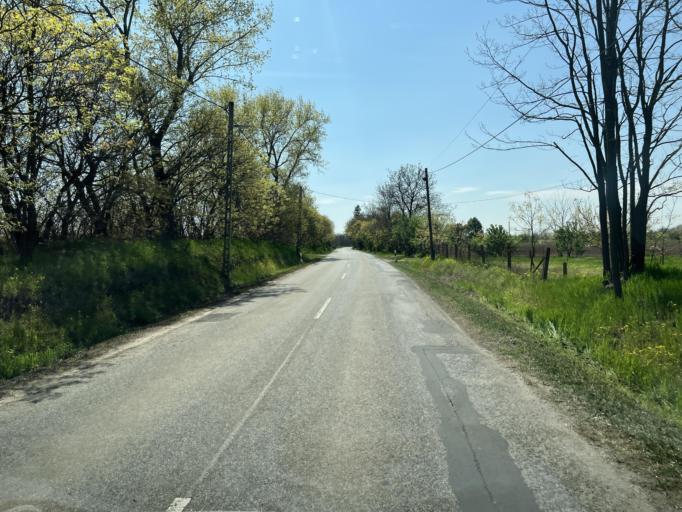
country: HU
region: Pest
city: Inarcs
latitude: 47.2435
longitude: 19.3170
